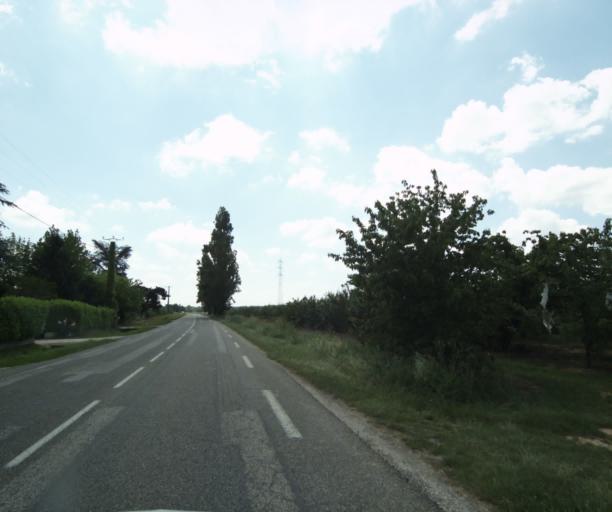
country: FR
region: Midi-Pyrenees
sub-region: Departement du Tarn-et-Garonne
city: Montauban
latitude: 44.0667
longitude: 1.3554
